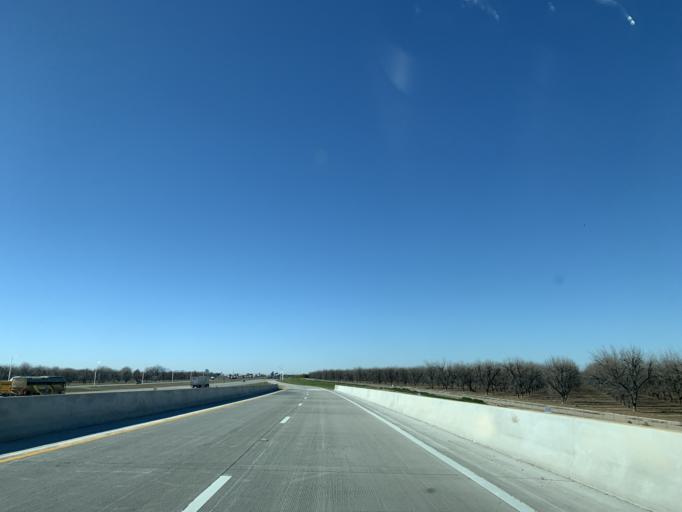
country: US
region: Arizona
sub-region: Pinal County
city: Eloy
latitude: 32.7279
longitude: -111.5216
